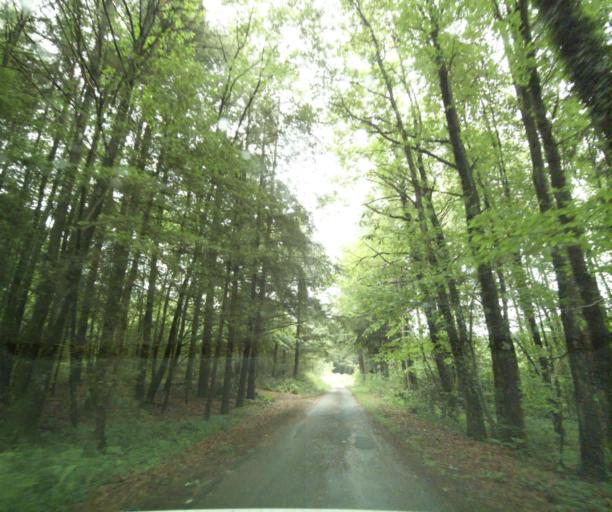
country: FR
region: Bourgogne
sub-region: Departement de Saone-et-Loire
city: Matour
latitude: 46.4506
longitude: 4.4650
